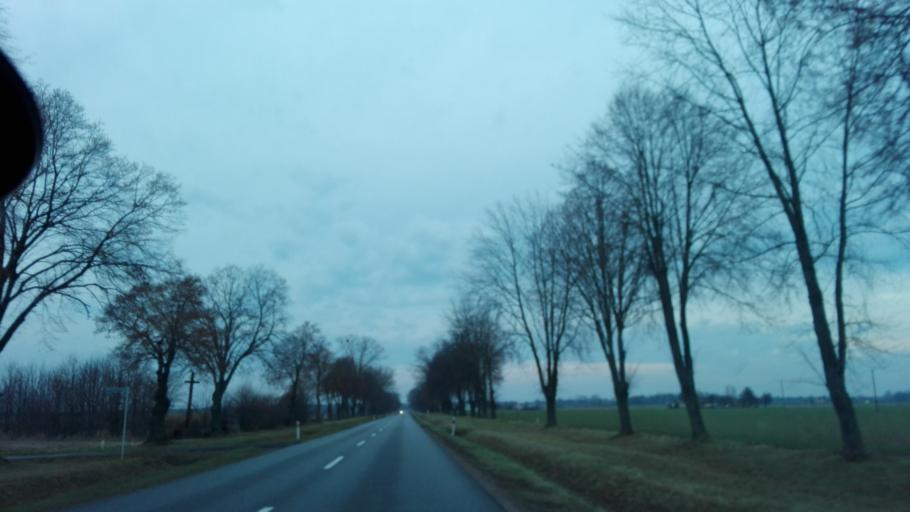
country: PL
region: Lublin Voivodeship
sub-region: Powiat radzynski
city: Wohyn
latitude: 51.7792
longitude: 22.7836
